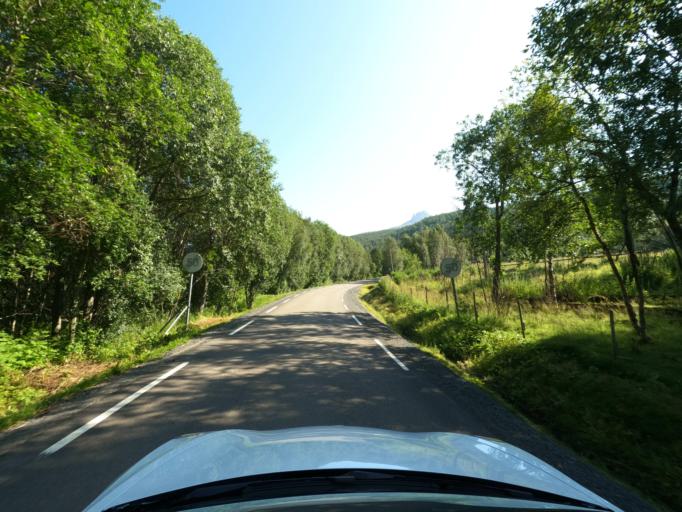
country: NO
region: Nordland
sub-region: Narvik
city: Narvik
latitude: 68.3964
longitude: 17.3020
